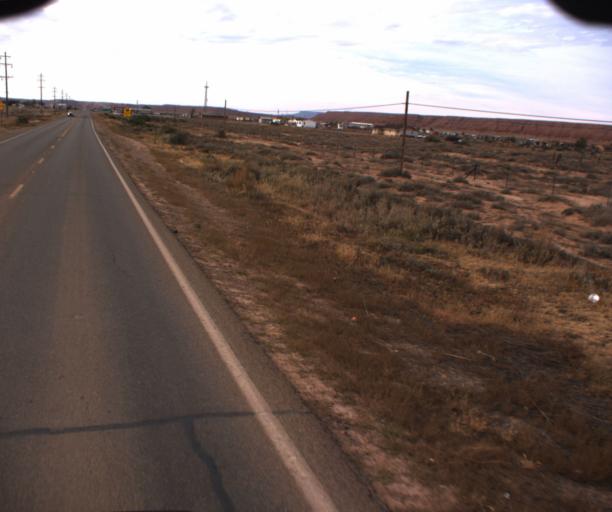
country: US
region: Arizona
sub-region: Apache County
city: Many Farms
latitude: 36.3586
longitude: -109.6156
